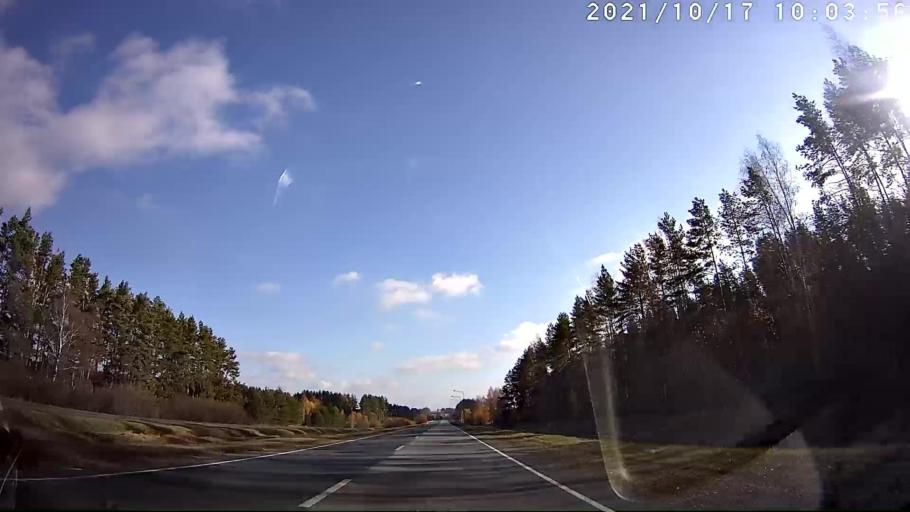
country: RU
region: Mariy-El
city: Sovetskiy
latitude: 56.7440
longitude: 48.2075
